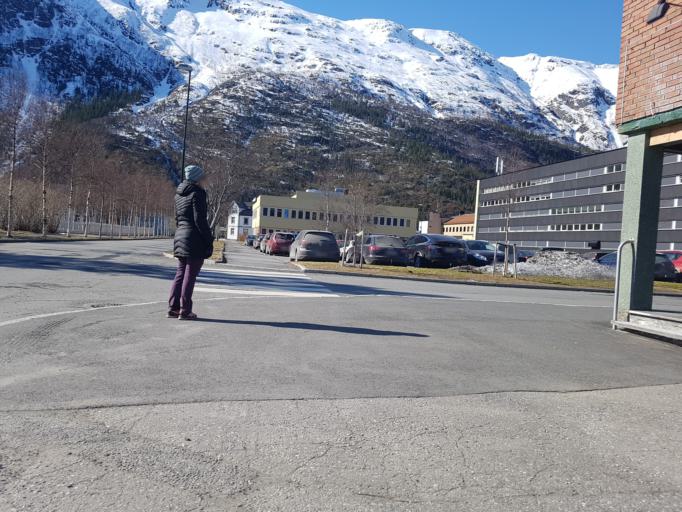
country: NO
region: Nordland
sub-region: Vefsn
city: Mosjoen
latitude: 65.8376
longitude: 13.1951
